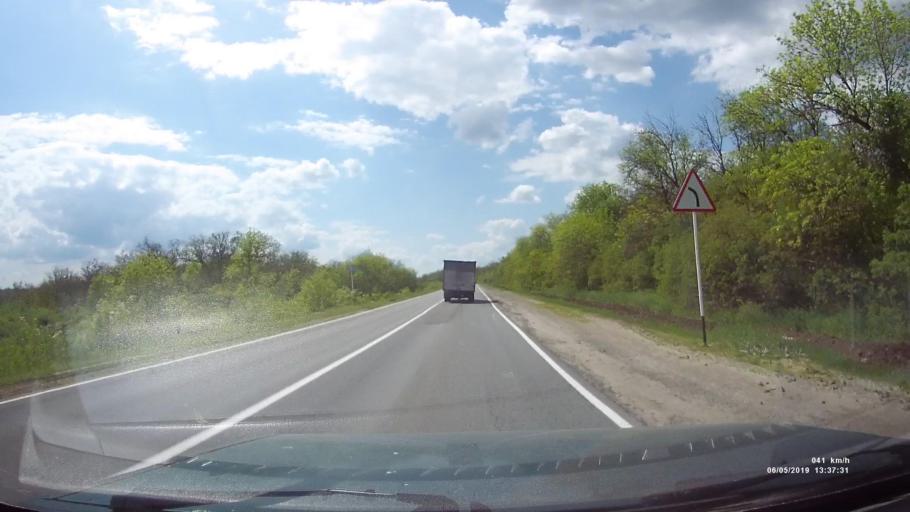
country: RU
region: Rostov
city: Ust'-Donetskiy
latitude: 47.6894
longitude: 40.7183
